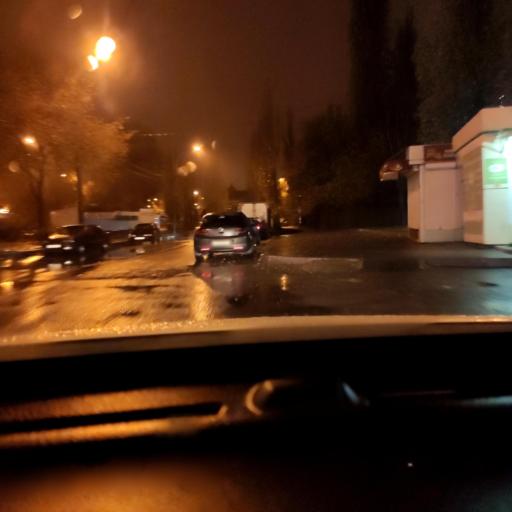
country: RU
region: Voronezj
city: Voronezh
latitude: 51.6513
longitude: 39.1430
